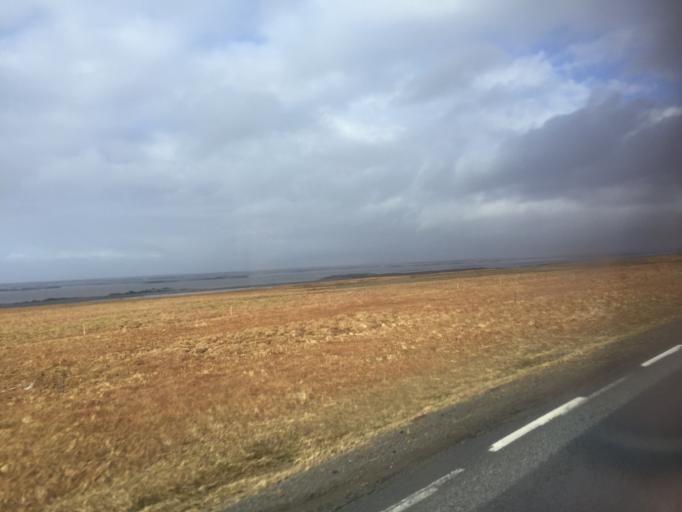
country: IS
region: West
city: Borgarnes
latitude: 64.4823
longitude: -21.9544
